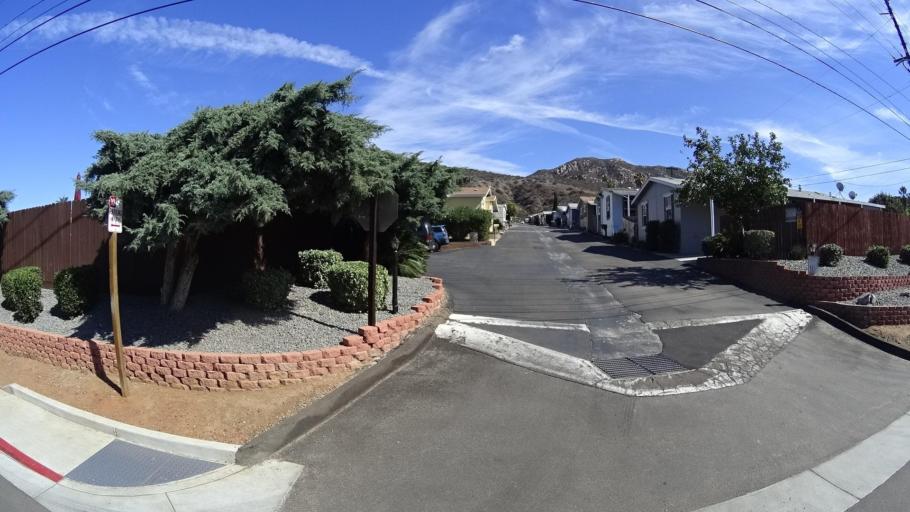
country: US
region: California
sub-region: San Diego County
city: Crest
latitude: 32.8384
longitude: -116.8743
